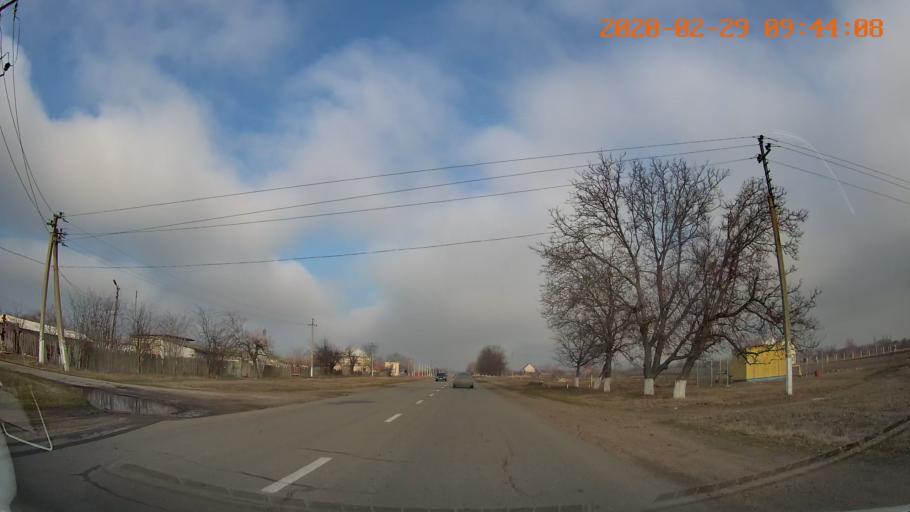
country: MD
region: Telenesti
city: Crasnoe
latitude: 46.6502
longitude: 29.8179
